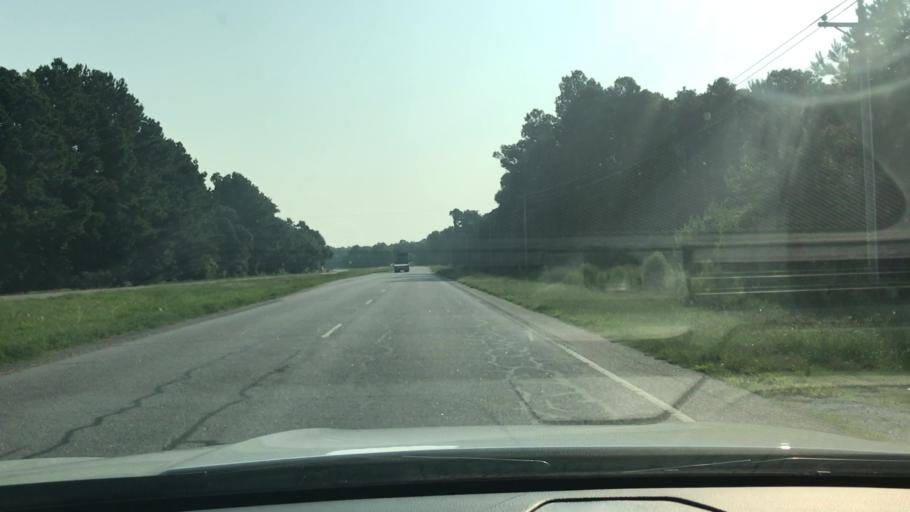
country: US
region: South Carolina
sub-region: Charleston County
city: Awendaw
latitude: 33.0533
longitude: -79.5506
